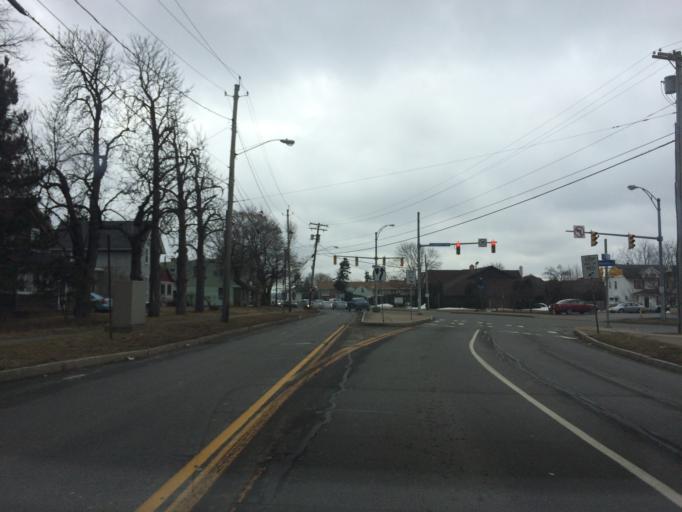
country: US
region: New York
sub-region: Monroe County
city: Rochester
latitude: 43.1174
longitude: -77.6168
